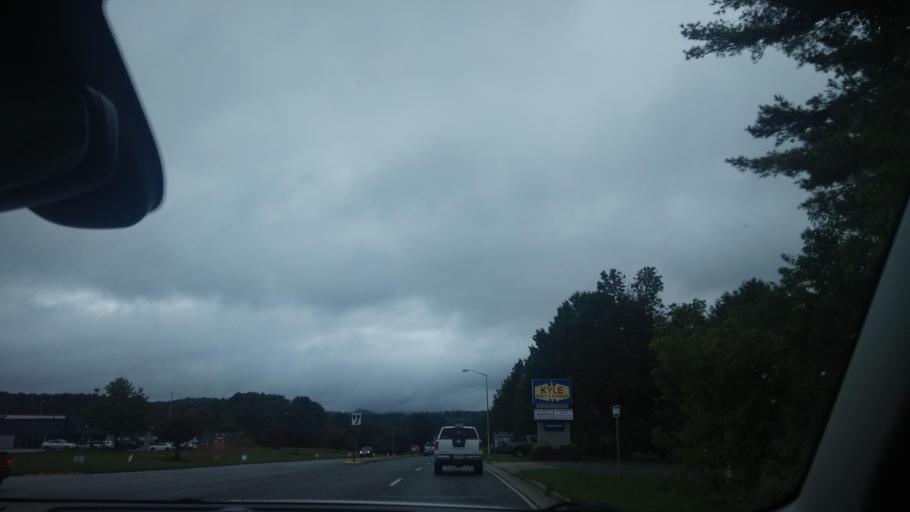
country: US
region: Virginia
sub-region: City of Galax
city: Galax
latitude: 36.6865
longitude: -80.8873
